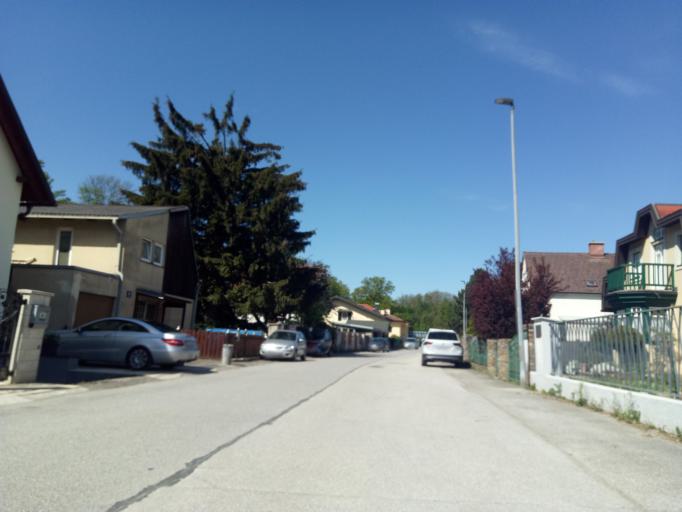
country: AT
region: Lower Austria
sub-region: Politischer Bezirk Modling
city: Kaltenleutgeben
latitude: 48.1344
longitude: 16.2129
